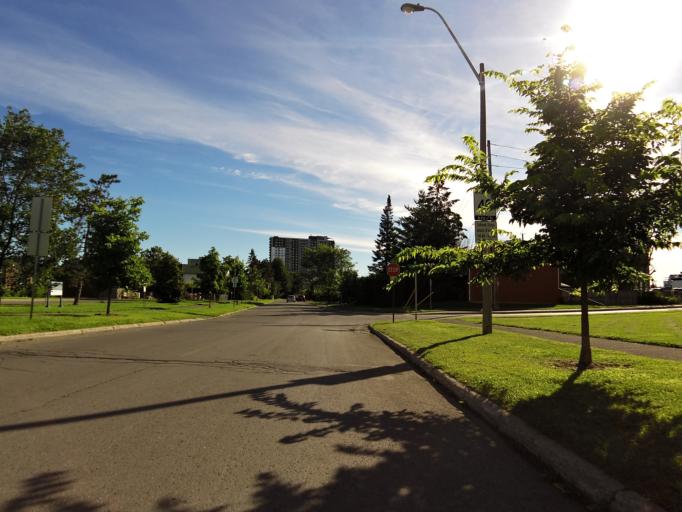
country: CA
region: Ontario
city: Bells Corners
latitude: 45.3663
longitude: -75.7905
